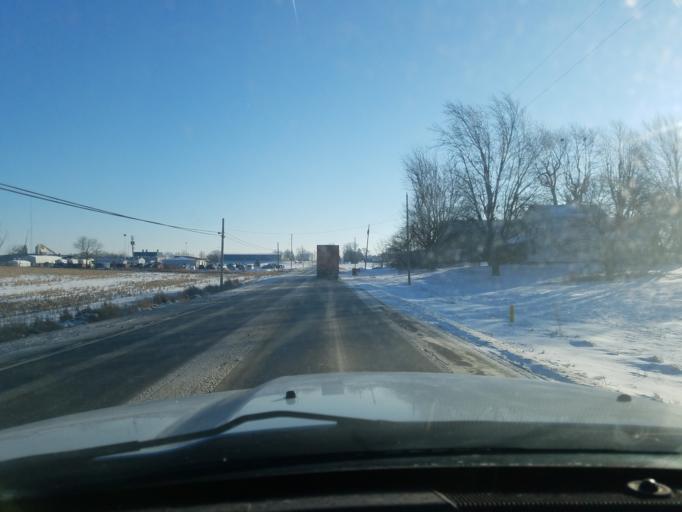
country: US
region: Indiana
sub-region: Noble County
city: Kendallville
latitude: 41.4524
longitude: -85.3150
